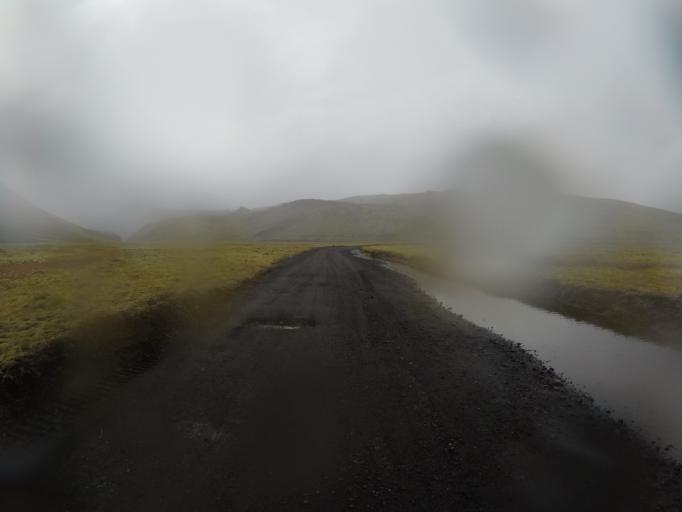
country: IS
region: South
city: Vestmannaeyjar
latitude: 63.9744
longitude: -18.8393
